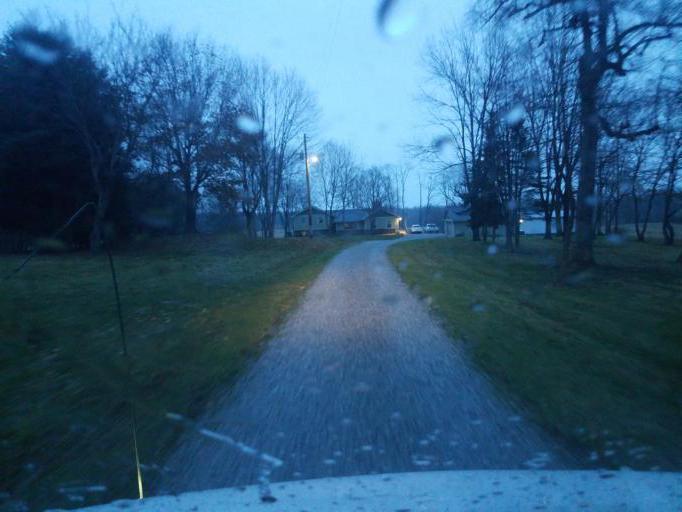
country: US
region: Ohio
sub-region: Licking County
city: Utica
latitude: 40.3134
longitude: -82.4536
